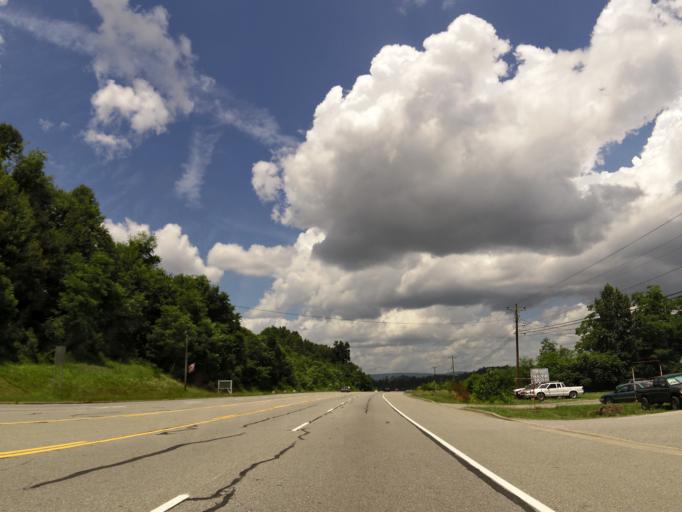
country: US
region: Tennessee
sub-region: Claiborne County
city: Tazewell
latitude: 36.4940
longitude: -83.5922
